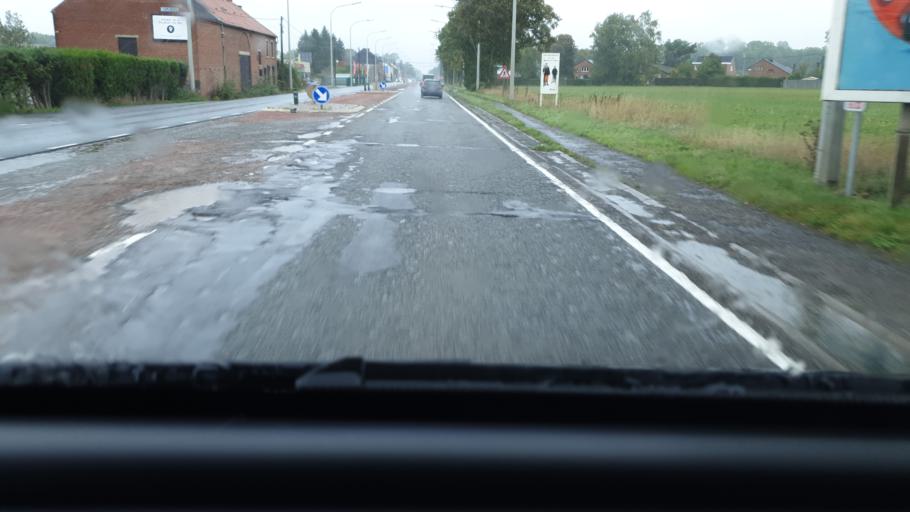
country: BE
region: Wallonia
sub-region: Province du Hainaut
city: Gerpinnes
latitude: 50.3163
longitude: 4.4787
